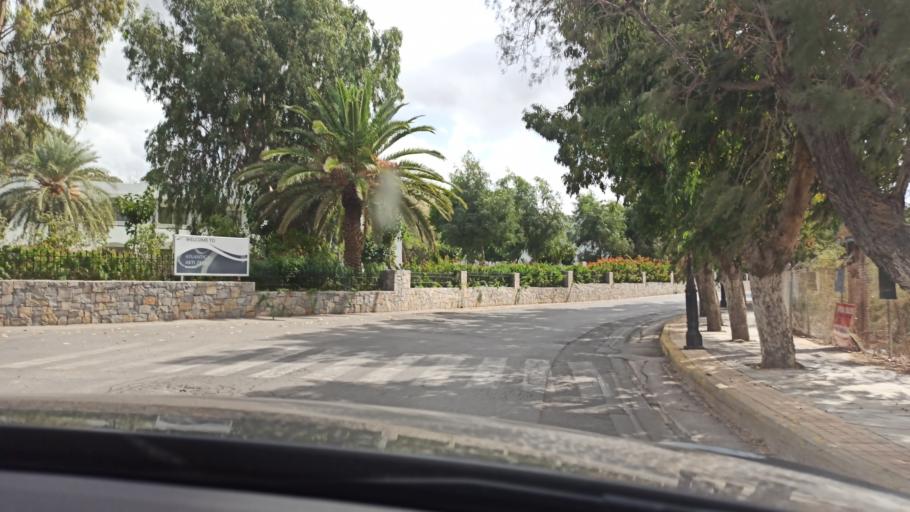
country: GR
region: Crete
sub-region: Nomos Irakleiou
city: Gazi
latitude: 35.3387
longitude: 25.0560
